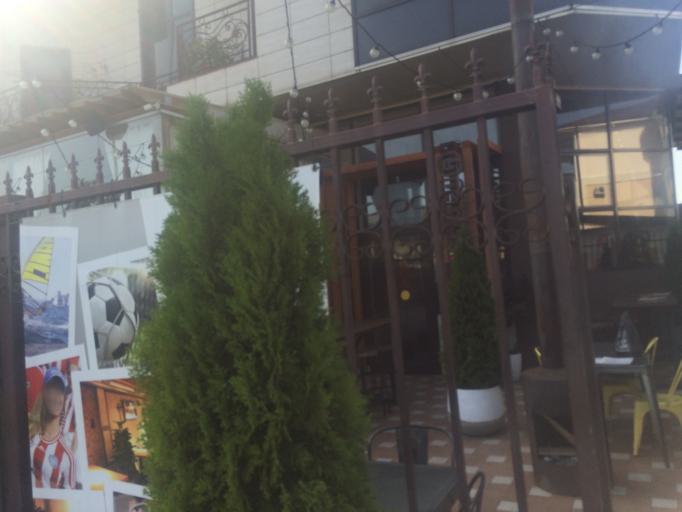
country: RU
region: Krasnodarskiy
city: Adler
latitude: 43.3919
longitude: 39.9865
